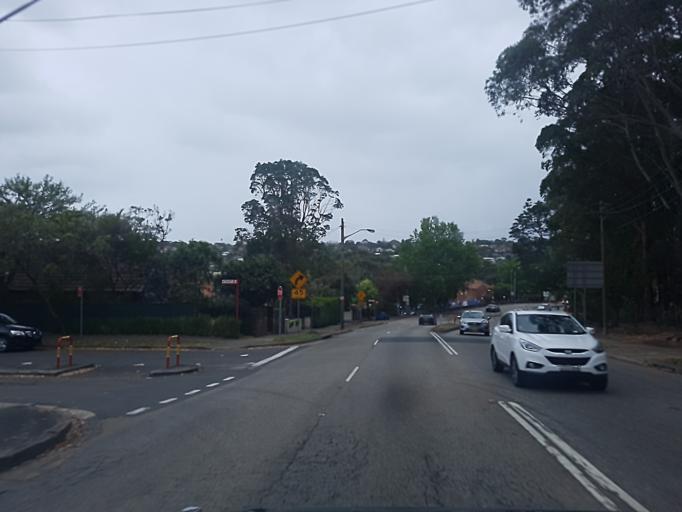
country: AU
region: New South Wales
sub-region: North Sydney
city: Cammeray
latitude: -33.8203
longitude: 151.2108
